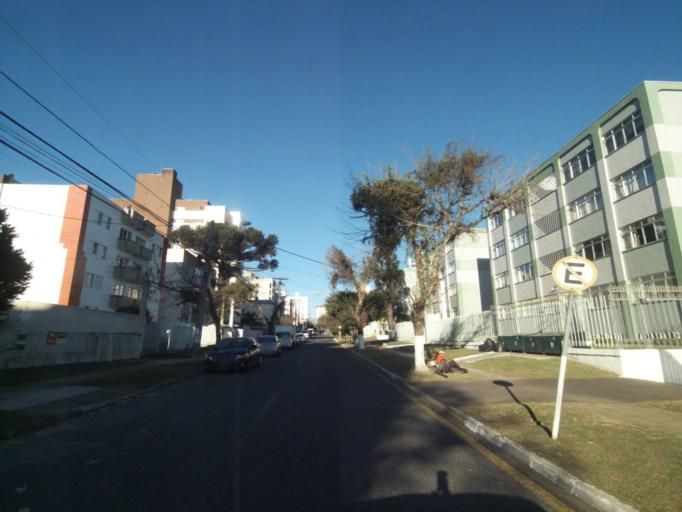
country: BR
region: Parana
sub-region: Curitiba
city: Curitiba
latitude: -25.4600
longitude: -49.2948
